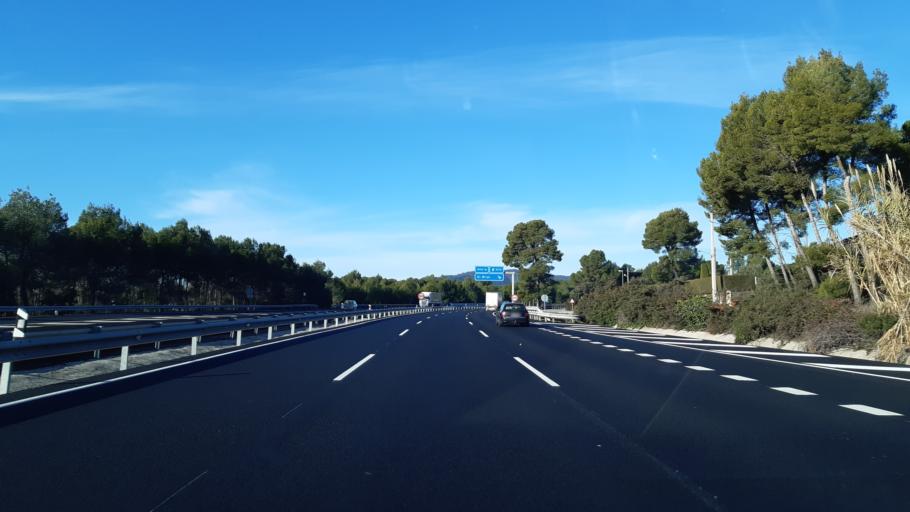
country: ES
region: Catalonia
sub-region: Provincia de Barcelona
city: Collbato
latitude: 41.5688
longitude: 1.8005
